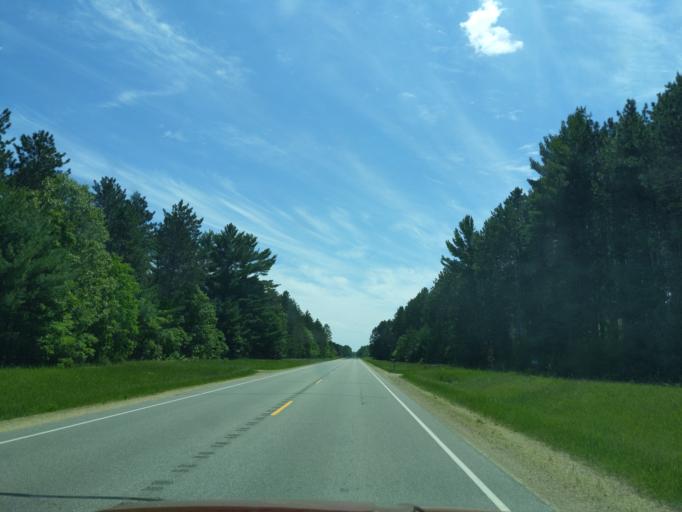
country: US
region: Wisconsin
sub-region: Marquette County
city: Montello
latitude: 43.9134
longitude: -89.3122
